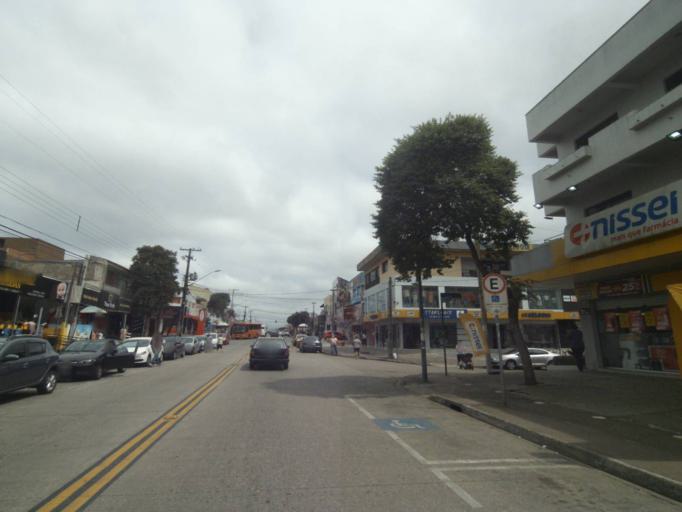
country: BR
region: Parana
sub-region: Sao Jose Dos Pinhais
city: Sao Jose dos Pinhais
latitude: -25.5445
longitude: -49.2597
